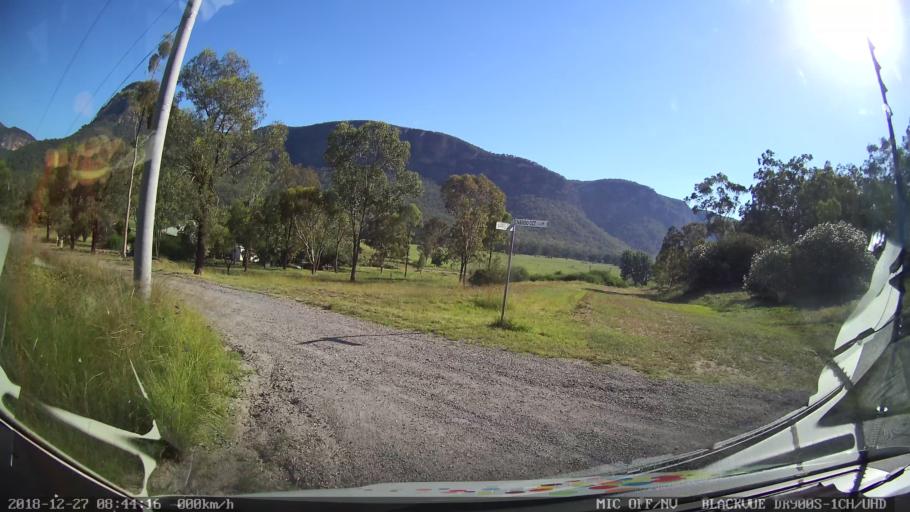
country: AU
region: New South Wales
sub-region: Lithgow
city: Portland
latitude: -33.1247
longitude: 150.2832
